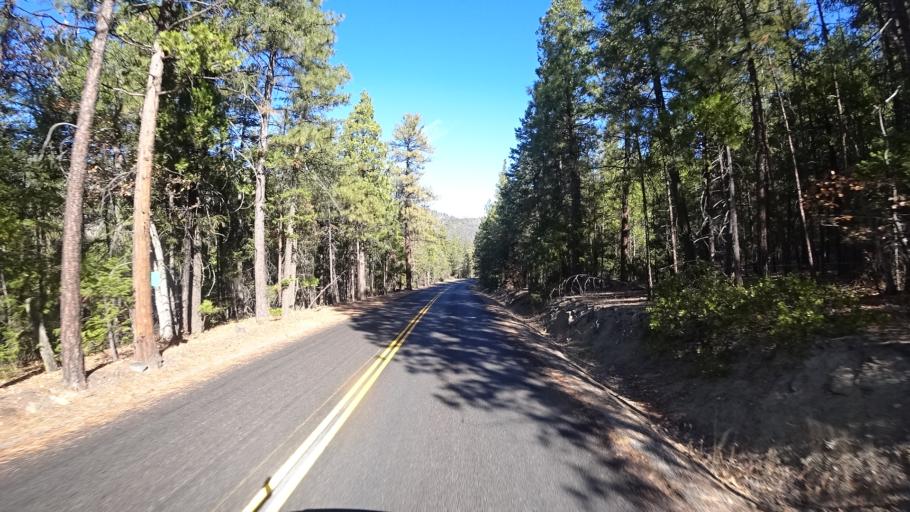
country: US
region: California
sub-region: Siskiyou County
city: Weed
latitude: 41.4294
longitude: -122.4975
